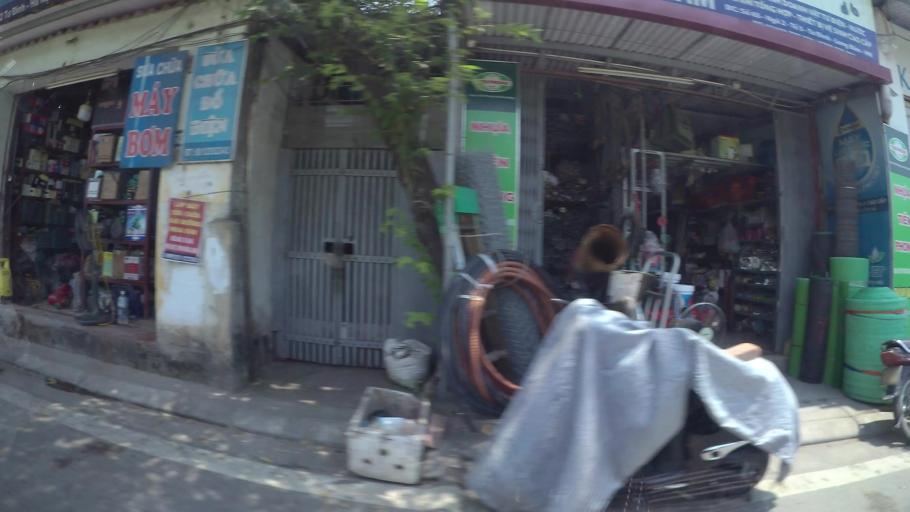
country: VN
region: Ha Noi
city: Hoan Kiem
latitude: 21.0261
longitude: 105.8839
